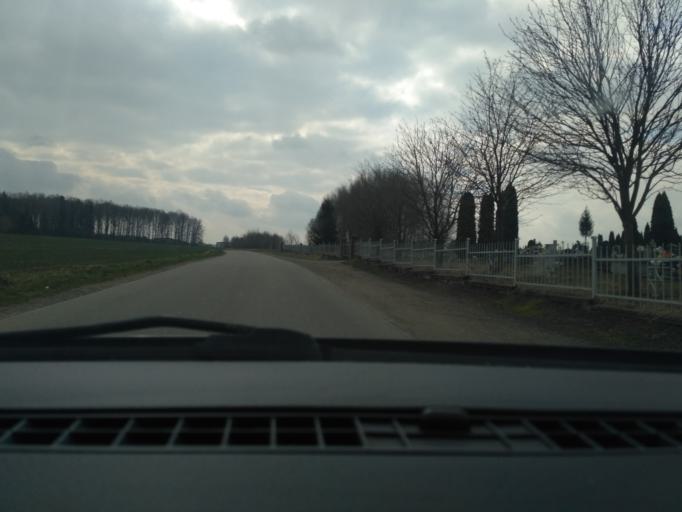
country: PL
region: Subcarpathian Voivodeship
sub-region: Powiat krosnienski
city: Kroscienko Wyzne
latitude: 49.6717
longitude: 21.8276
